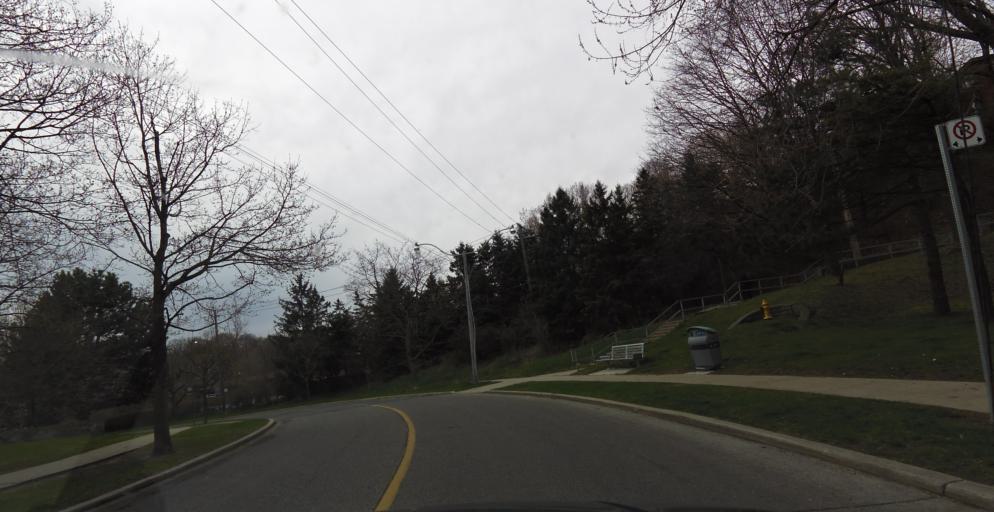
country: CA
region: Ontario
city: Toronto
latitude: 43.6399
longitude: -79.4742
